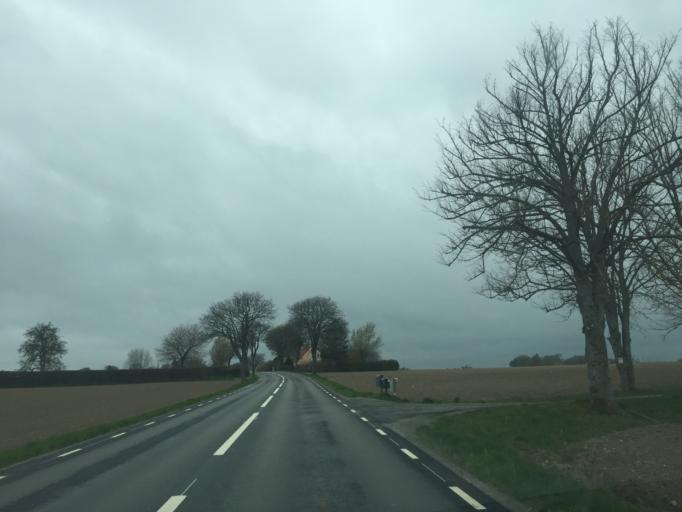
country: SE
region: Skane
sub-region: Skurups Kommun
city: Skivarp
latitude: 55.4235
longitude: 13.6073
